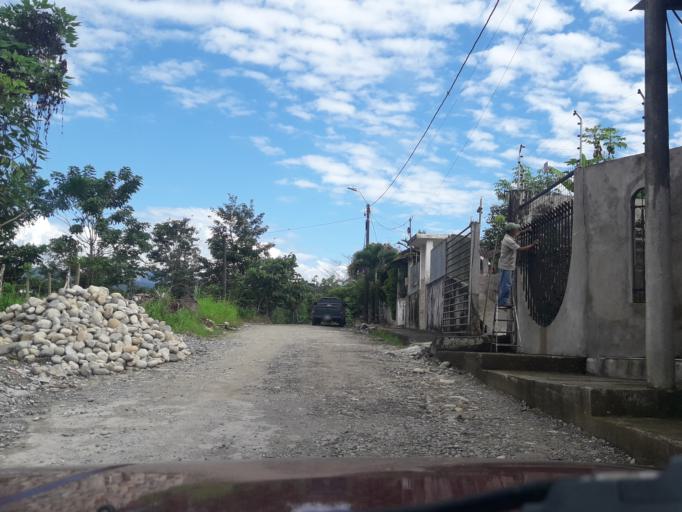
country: EC
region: Napo
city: Tena
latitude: -0.9834
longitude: -77.8212
